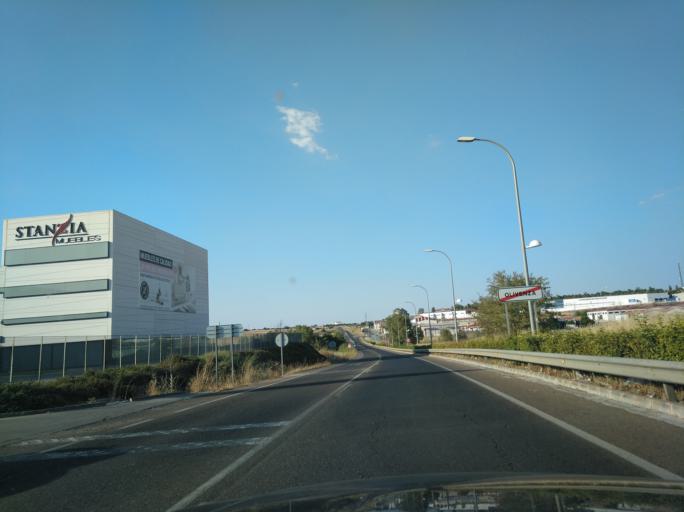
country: ES
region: Extremadura
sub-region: Provincia de Badajoz
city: Olivenza
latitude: 38.6921
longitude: -7.0923
